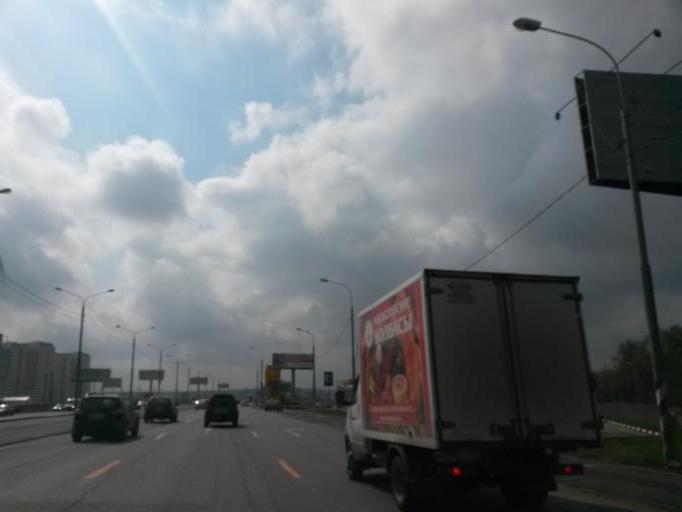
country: RU
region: Moscow
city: Annino
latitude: 55.5370
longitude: 37.6097
